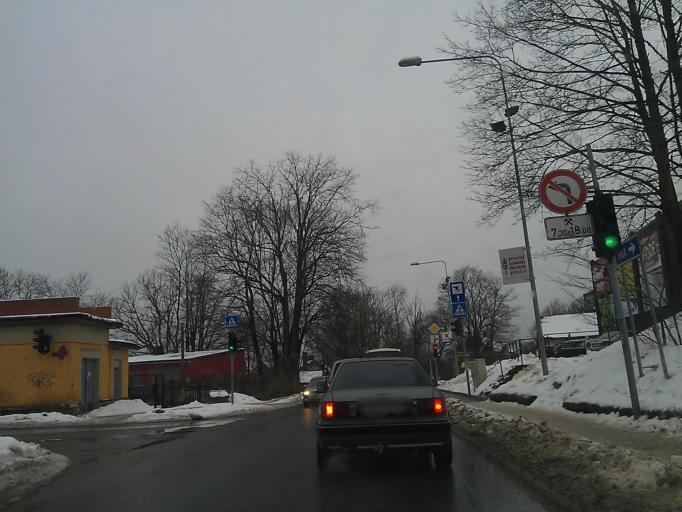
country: LV
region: Cesu Rajons
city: Cesis
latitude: 57.3088
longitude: 25.2773
